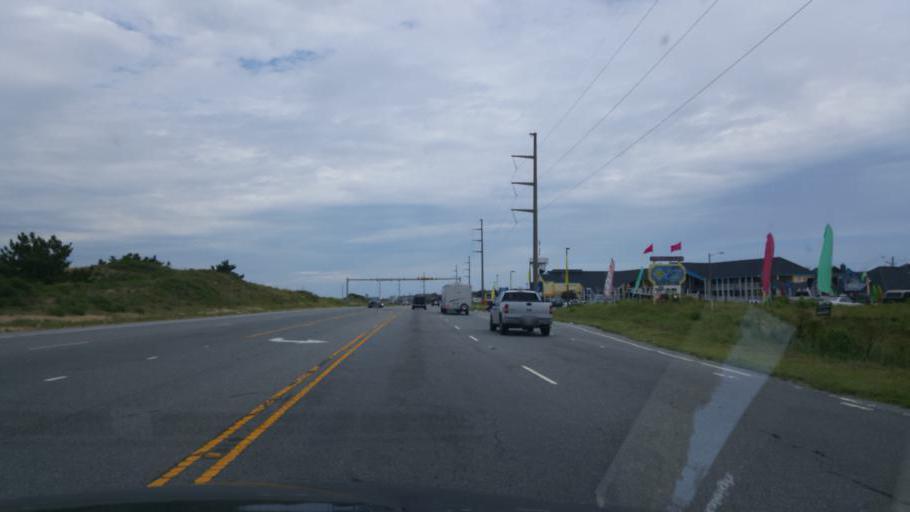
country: US
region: North Carolina
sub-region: Dare County
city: Nags Head
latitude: 35.9570
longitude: -75.6257
